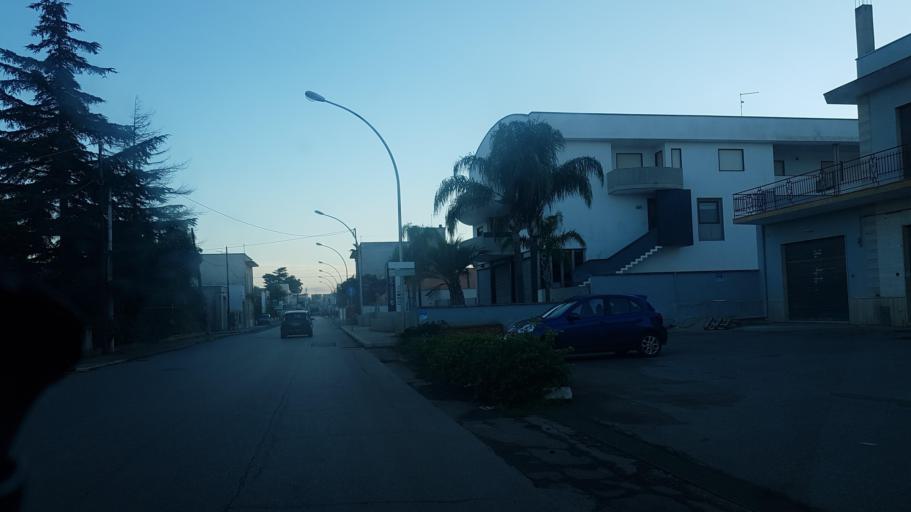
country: IT
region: Apulia
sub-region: Provincia di Brindisi
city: San Michele Salentino
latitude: 40.6353
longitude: 17.6321
